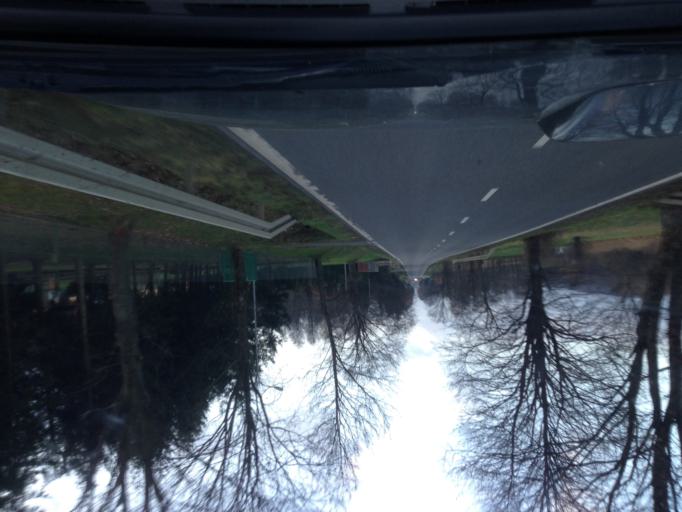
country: PL
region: Subcarpathian Voivodeship
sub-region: Powiat jasielski
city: Osiek Jasielski
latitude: 49.6450
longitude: 21.5143
